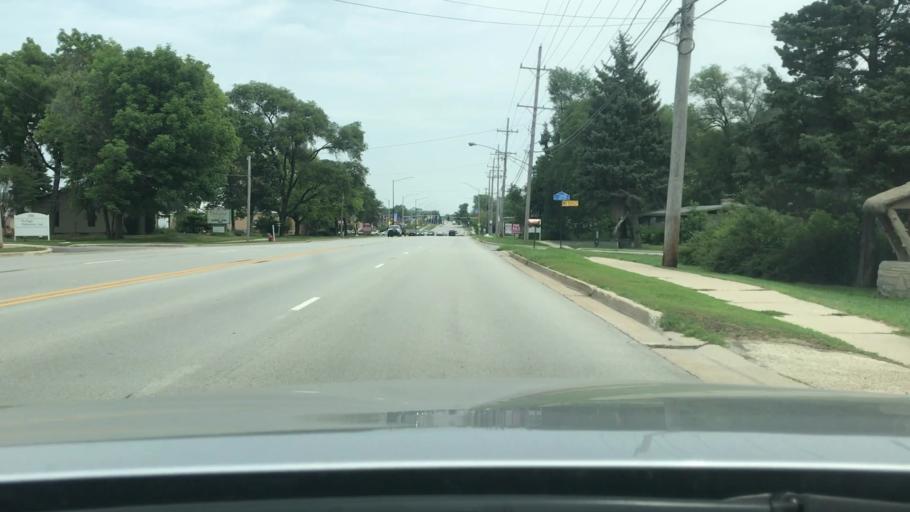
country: US
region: Illinois
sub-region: DuPage County
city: Darien
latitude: 41.7484
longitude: -87.9770
